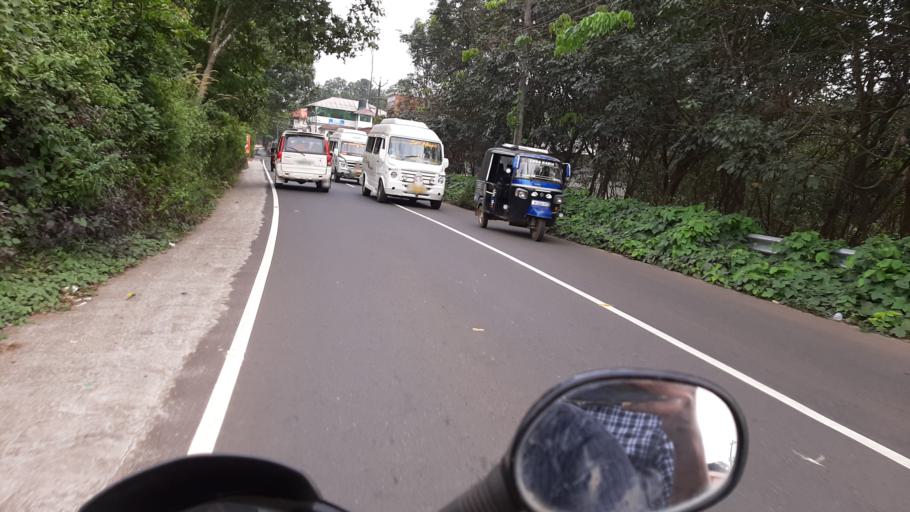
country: IN
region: Kerala
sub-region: Pattanamtitta
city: Pathanamthitta
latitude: 9.4482
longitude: 76.8727
